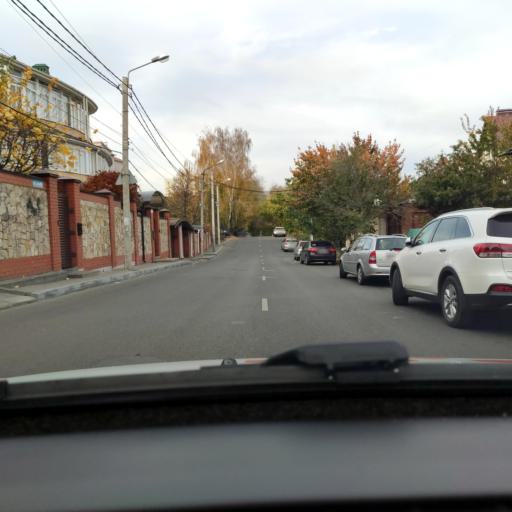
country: RU
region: Voronezj
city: Voronezh
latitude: 51.6662
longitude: 39.2144
